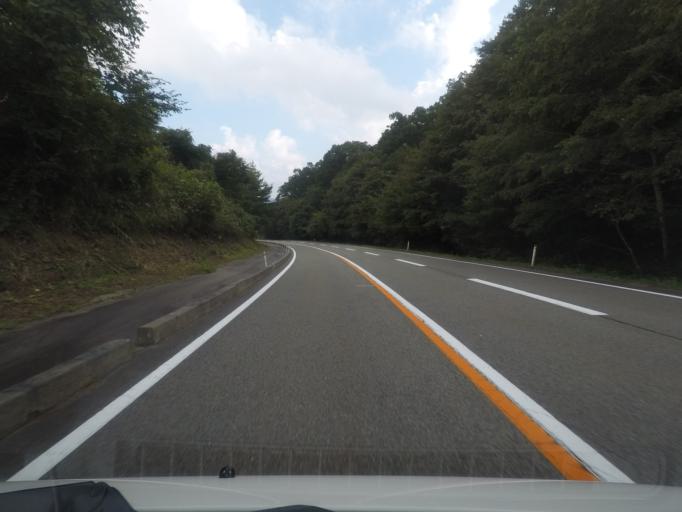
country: JP
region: Fukushima
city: Funehikimachi-funehiki
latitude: 37.5777
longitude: 140.7248
